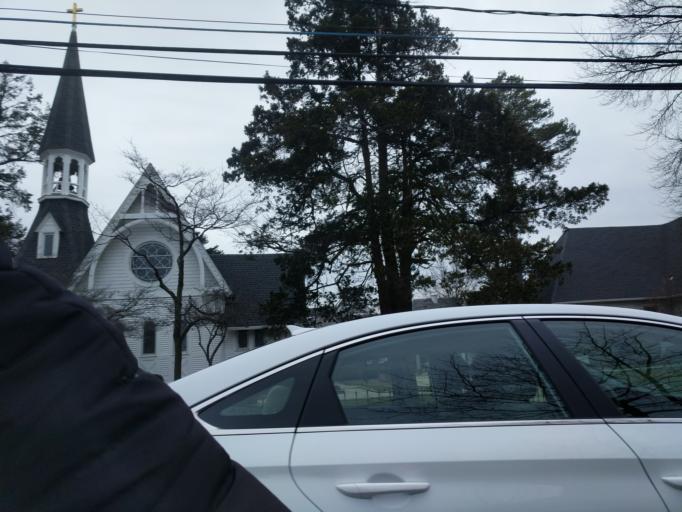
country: US
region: New York
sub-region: Nassau County
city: Woodmere
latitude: 40.6341
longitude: -73.7050
